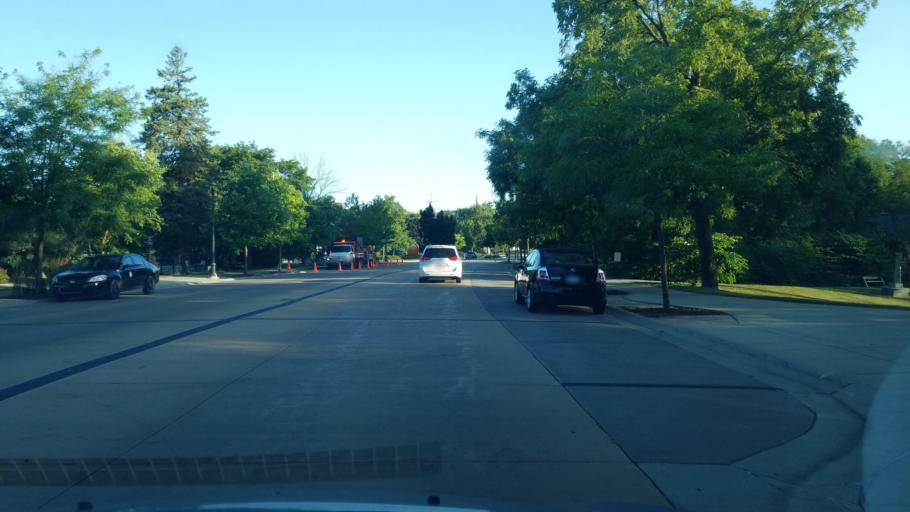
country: US
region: Wisconsin
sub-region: Ozaukee County
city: Mequon
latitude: 43.2236
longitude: -87.9838
